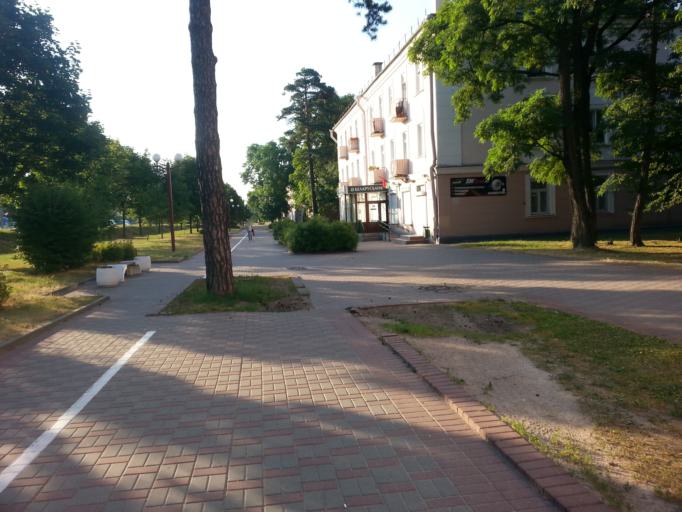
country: BY
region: Minsk
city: Vyaliki Trastsyanets
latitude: 53.8675
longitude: 27.6529
